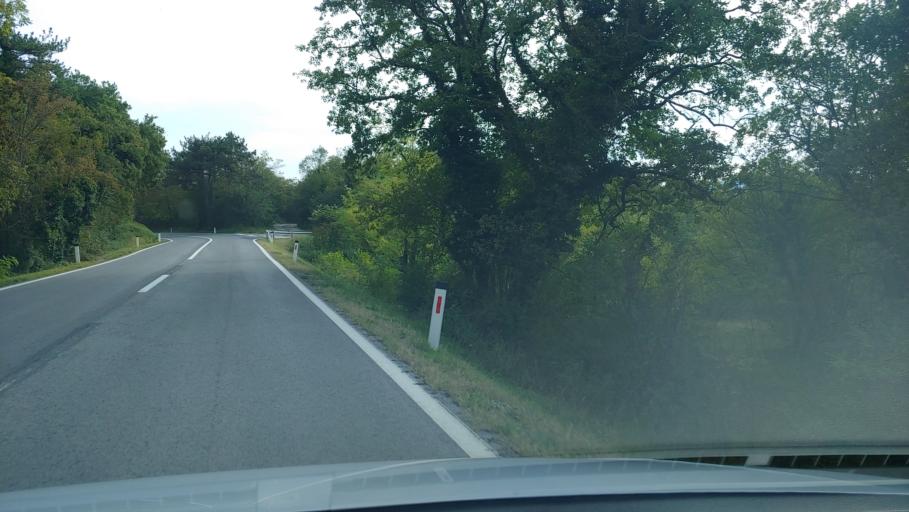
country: SI
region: Nova Gorica
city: Sempas
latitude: 45.9014
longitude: 13.7807
